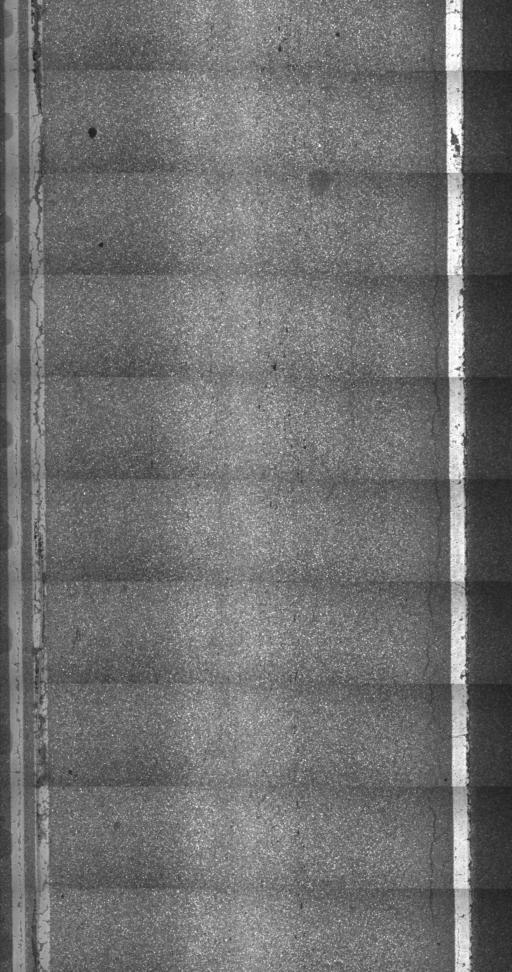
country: US
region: Vermont
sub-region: Chittenden County
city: Colchester
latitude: 44.5419
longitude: -73.1465
